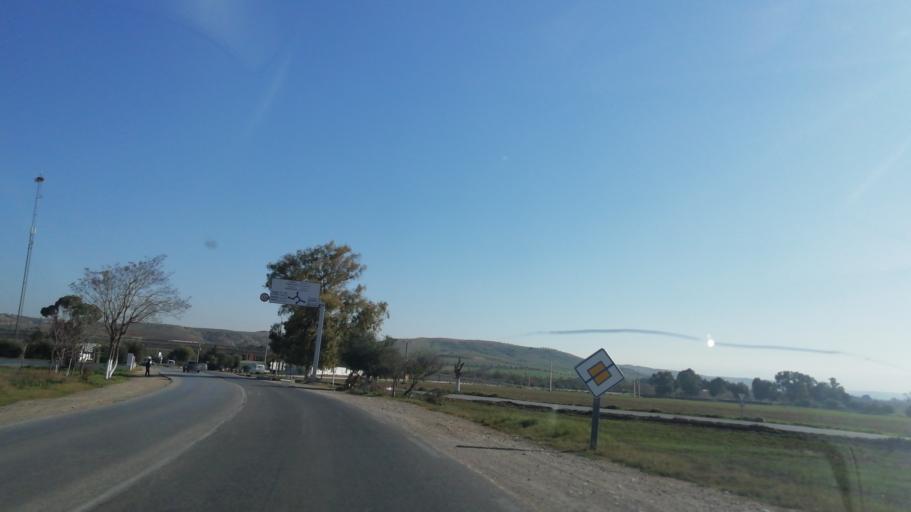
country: DZ
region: Tlemcen
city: Remchi
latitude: 35.0475
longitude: -1.5067
